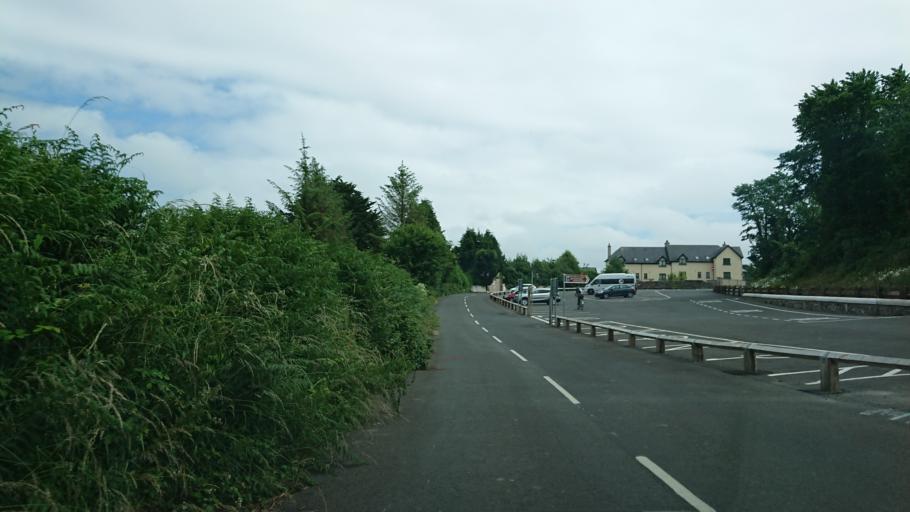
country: IE
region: Munster
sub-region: Waterford
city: Waterford
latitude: 52.2704
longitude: -7.1387
